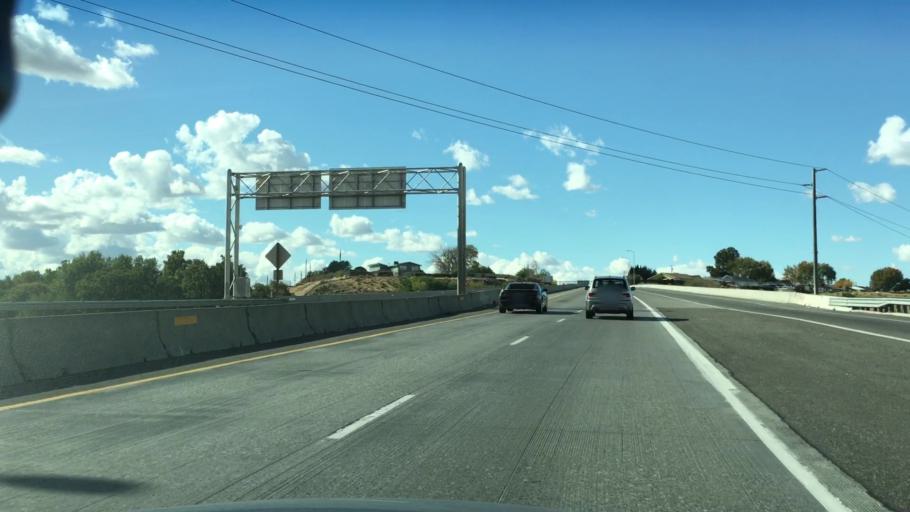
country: US
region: Washington
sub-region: Benton County
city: Kennewick
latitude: 46.2199
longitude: -119.1365
